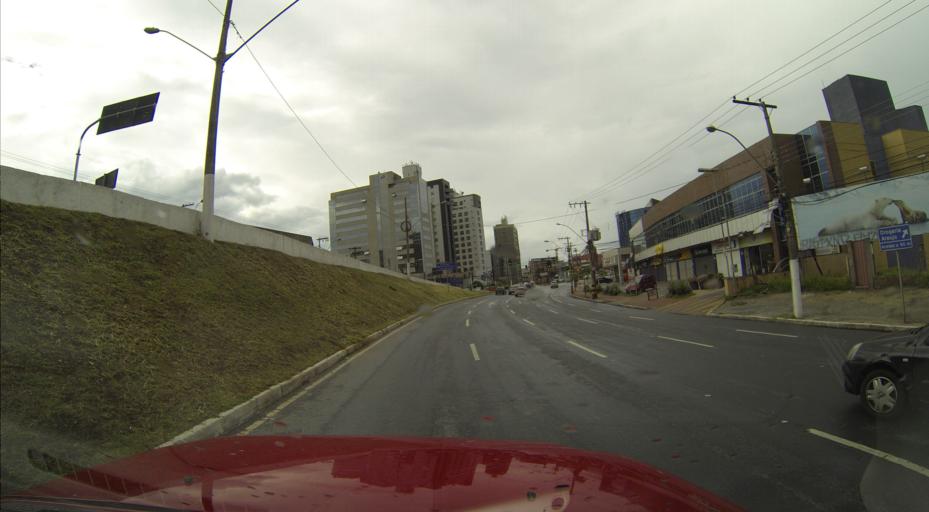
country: BR
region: Minas Gerais
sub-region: Belo Horizonte
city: Belo Horizonte
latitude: -19.9697
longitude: -43.9541
